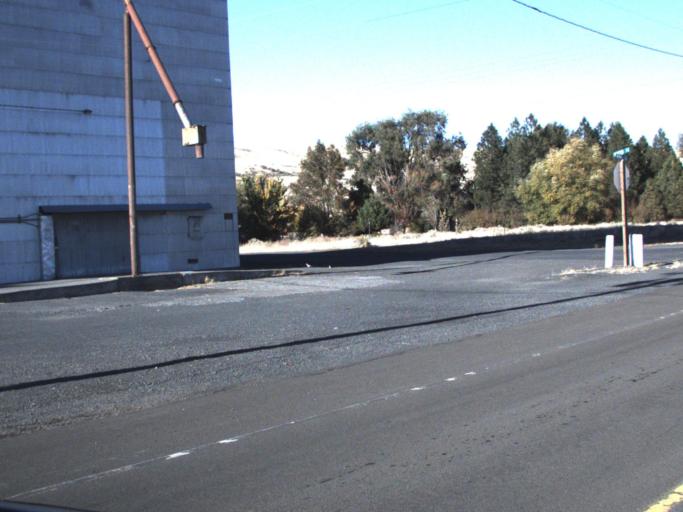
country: US
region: Washington
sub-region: Adams County
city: Ritzville
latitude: 46.7559
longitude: -118.3108
